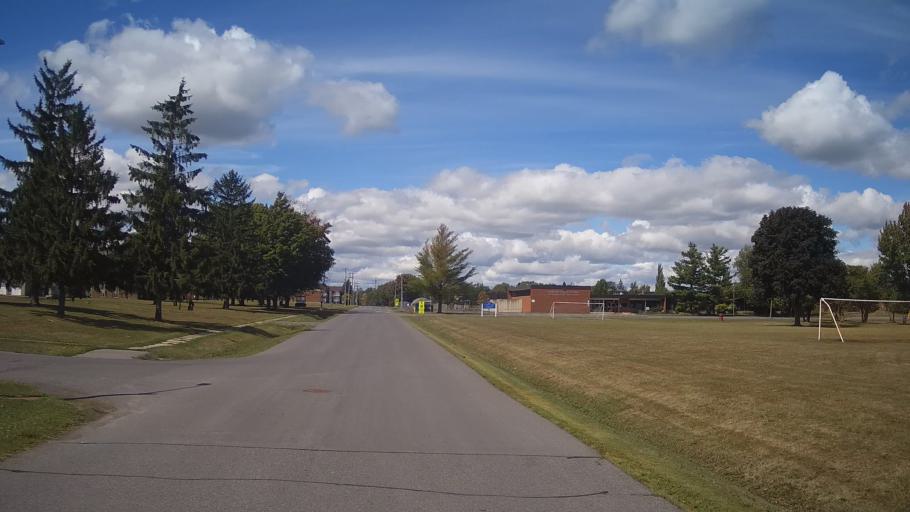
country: US
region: New York
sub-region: St. Lawrence County
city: Ogdensburg
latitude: 44.8475
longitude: -75.3127
